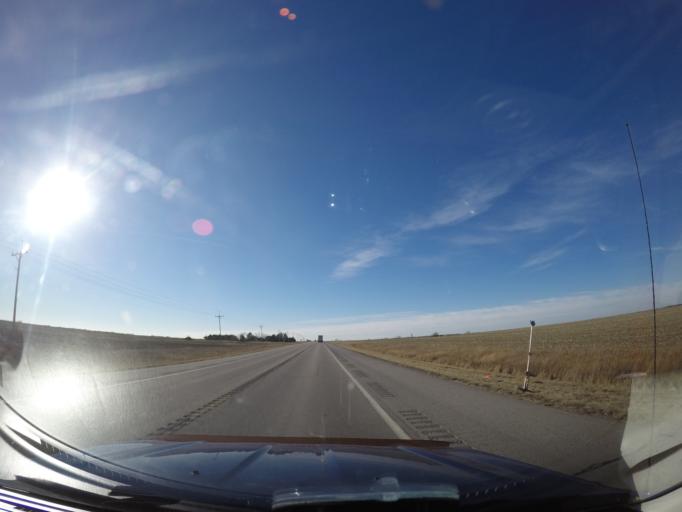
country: US
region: Kansas
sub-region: Marion County
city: Hillsboro
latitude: 38.3626
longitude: -97.2656
